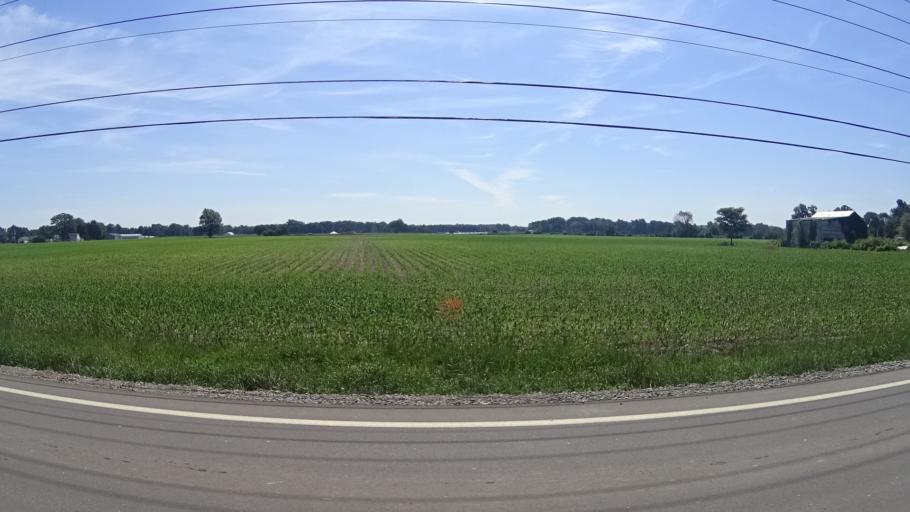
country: US
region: Ohio
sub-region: Erie County
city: Huron
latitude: 41.3754
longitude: -82.4928
